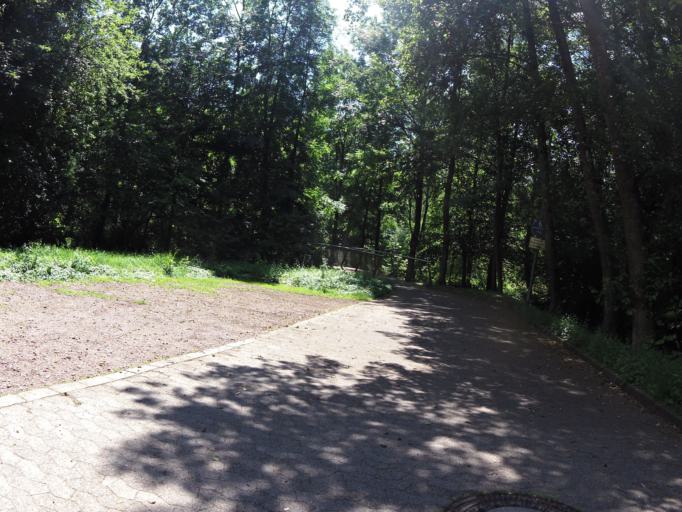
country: DE
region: Baden-Wuerttemberg
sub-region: Freiburg Region
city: Hohberg
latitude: 48.3394
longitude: 7.8984
